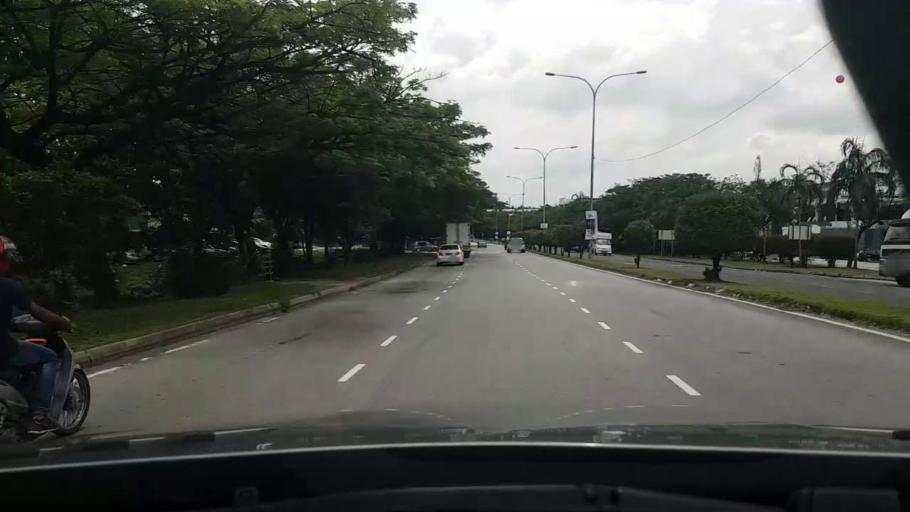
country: MY
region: Putrajaya
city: Putrajaya
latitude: 2.9811
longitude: 101.6299
